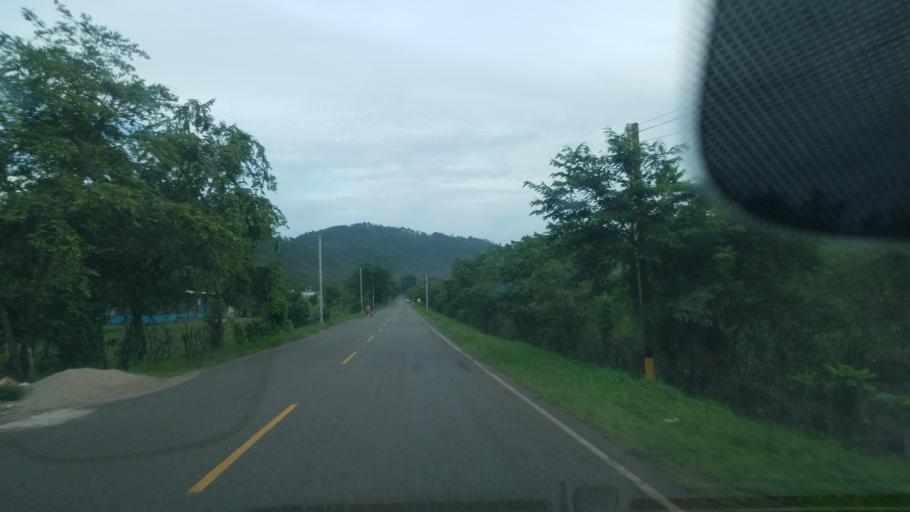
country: HN
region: Santa Barbara
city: San Vicente Centenario
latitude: 14.8639
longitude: -88.2484
